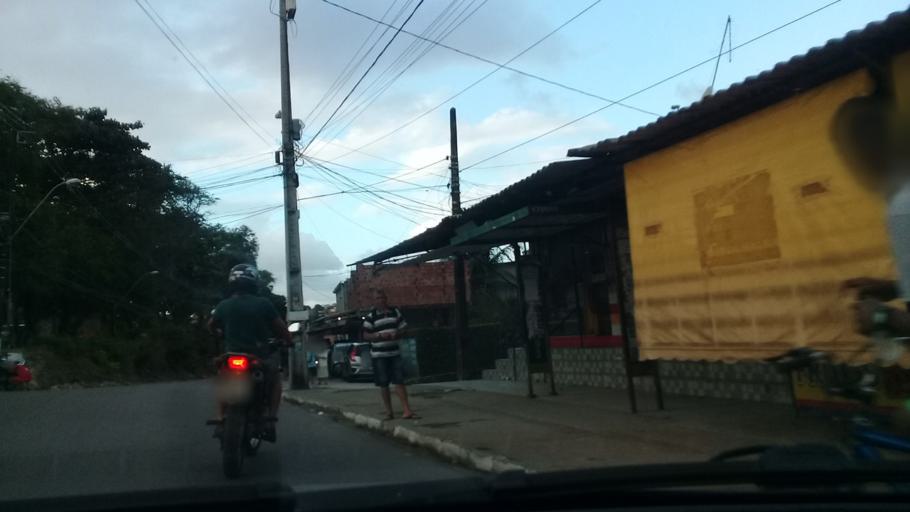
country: BR
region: Pernambuco
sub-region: Jaboatao Dos Guararapes
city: Jaboatao dos Guararapes
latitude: -8.1310
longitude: -34.9496
